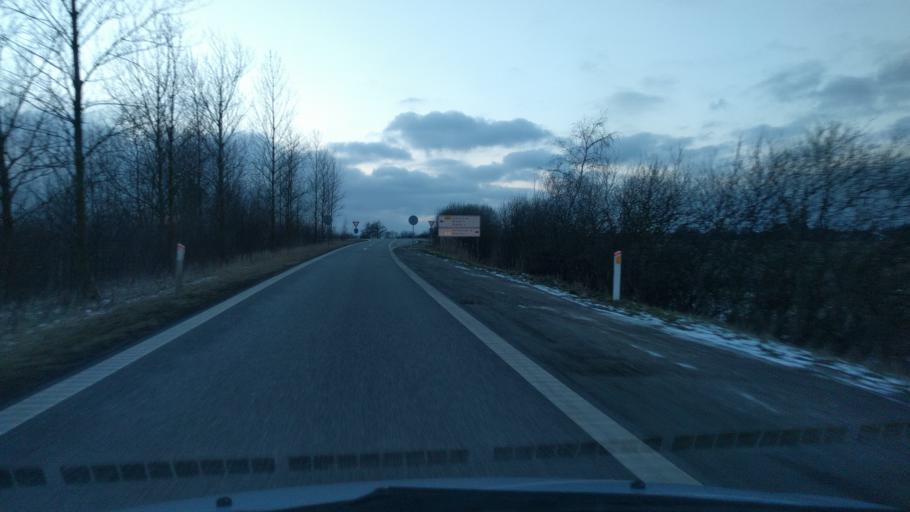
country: DK
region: South Denmark
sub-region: Nyborg Kommune
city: Nyborg
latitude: 55.3320
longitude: 10.7433
